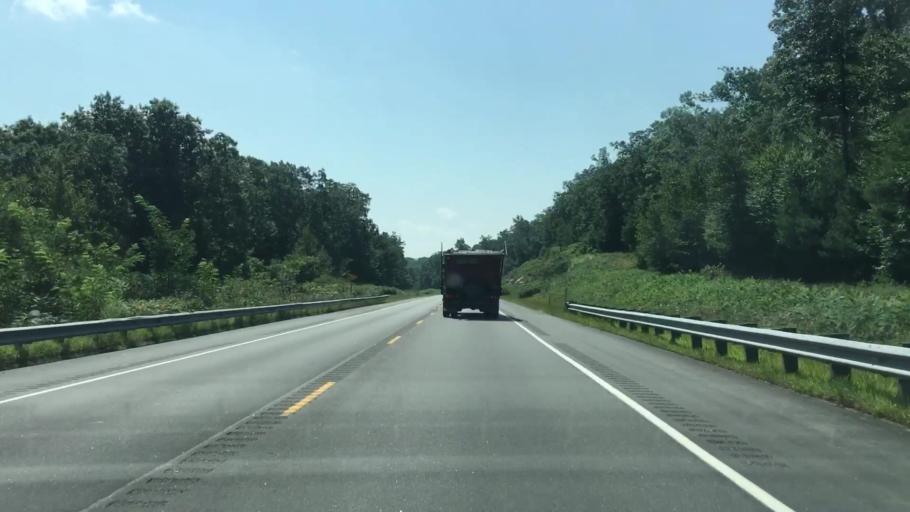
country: US
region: New Hampshire
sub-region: Rockingham County
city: Salem
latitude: 42.8220
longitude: -71.2439
